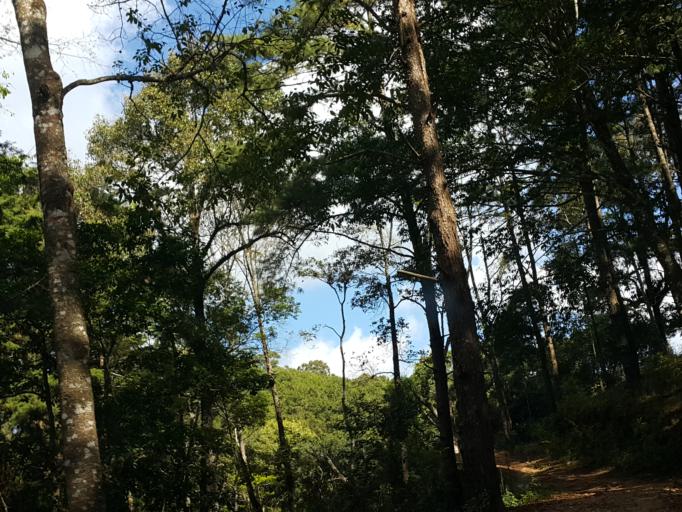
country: TH
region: Chiang Mai
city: Wiang Haeng
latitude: 19.5336
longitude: 98.8098
